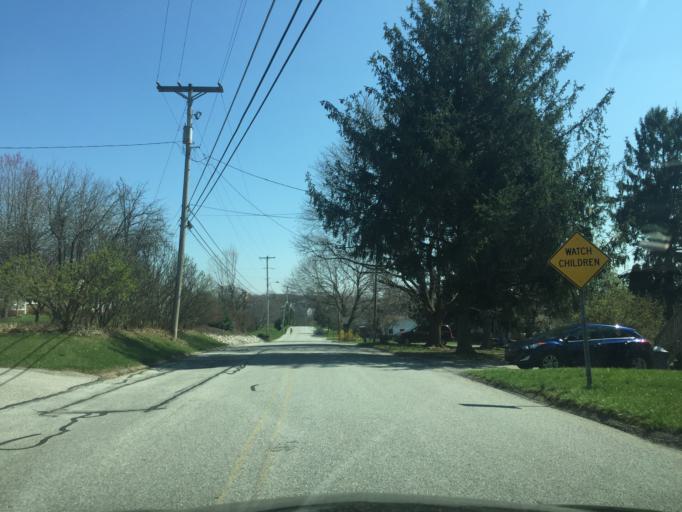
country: US
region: Pennsylvania
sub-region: York County
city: New Freedom
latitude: 39.7293
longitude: -76.6995
